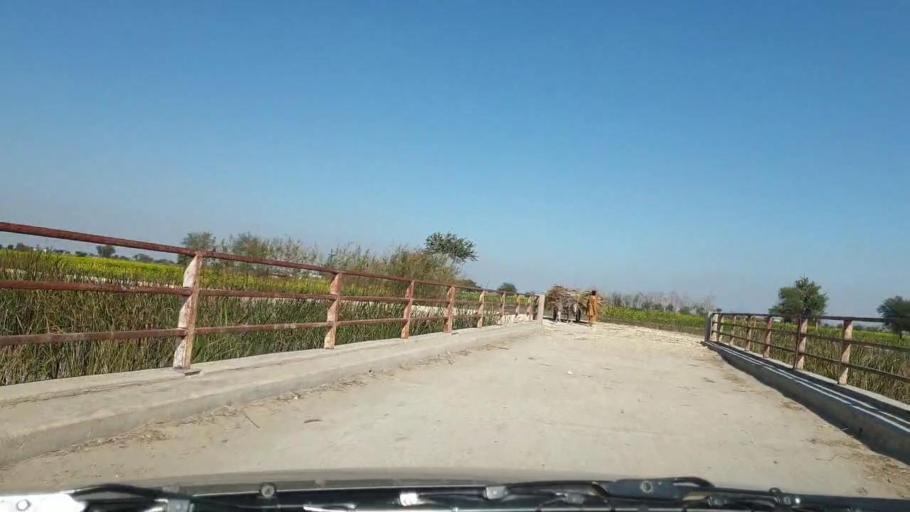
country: PK
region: Sindh
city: Khadro
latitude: 26.1478
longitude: 68.7717
